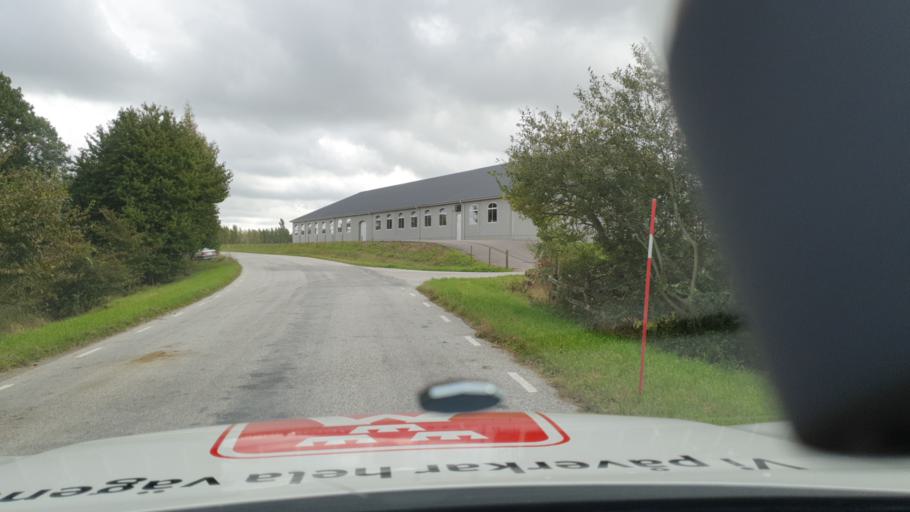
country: SE
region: Skane
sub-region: Malmo
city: Oxie
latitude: 55.5124
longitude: 13.1121
